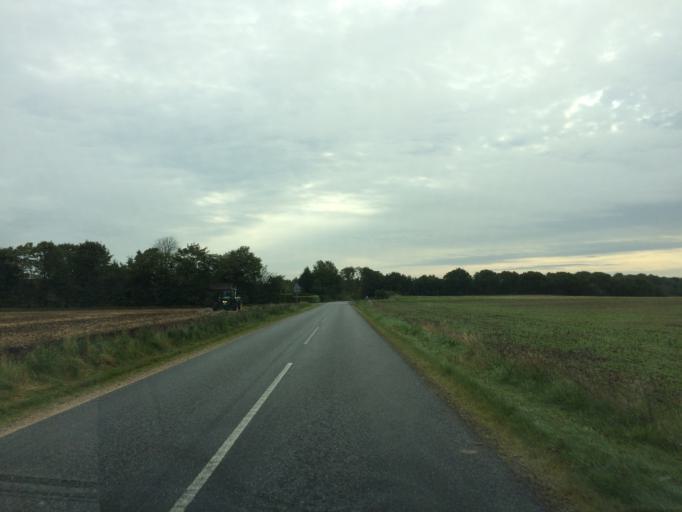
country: DK
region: Central Jutland
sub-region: Herning Kommune
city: Lind
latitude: 56.0894
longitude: 8.9504
